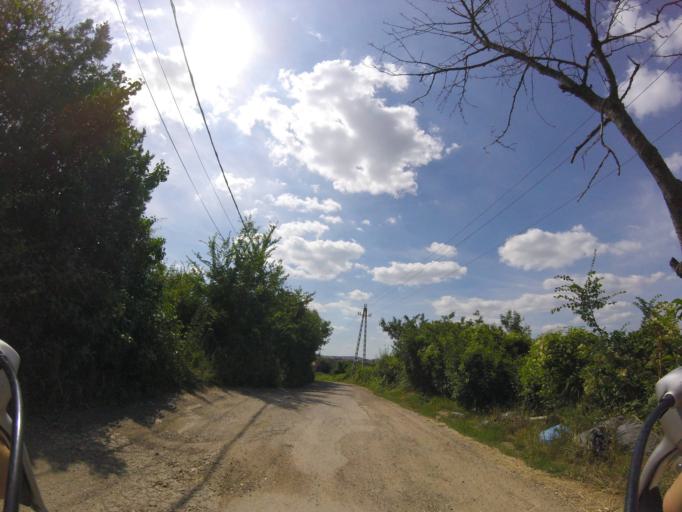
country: HU
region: Pest
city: Budaors
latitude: 47.4388
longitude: 18.9433
